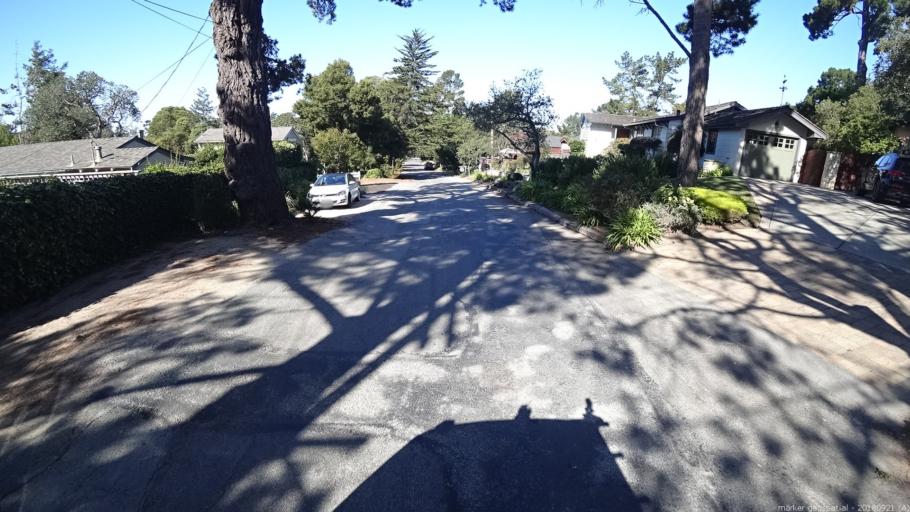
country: US
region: California
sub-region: Monterey County
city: Carmel-by-the-Sea
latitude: 36.5618
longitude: -121.9141
